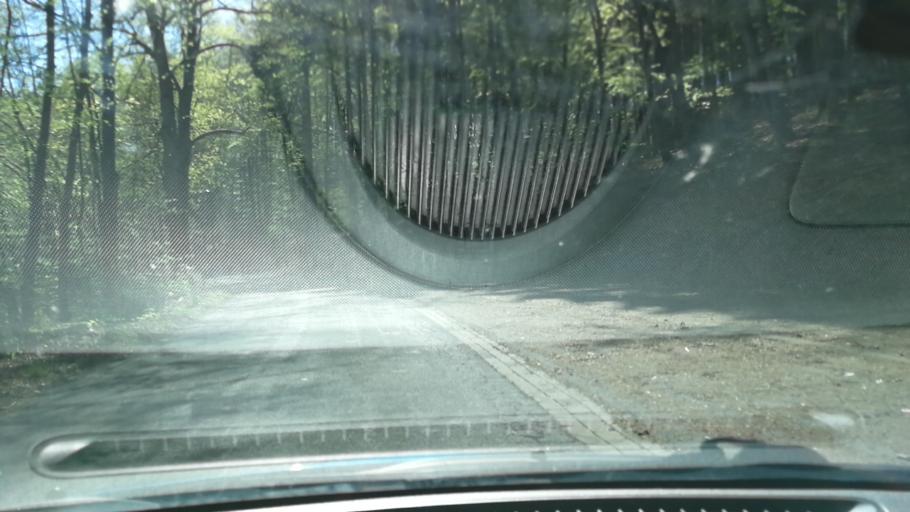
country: DE
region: Lower Saxony
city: Buhren
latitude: 51.5198
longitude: 9.6937
